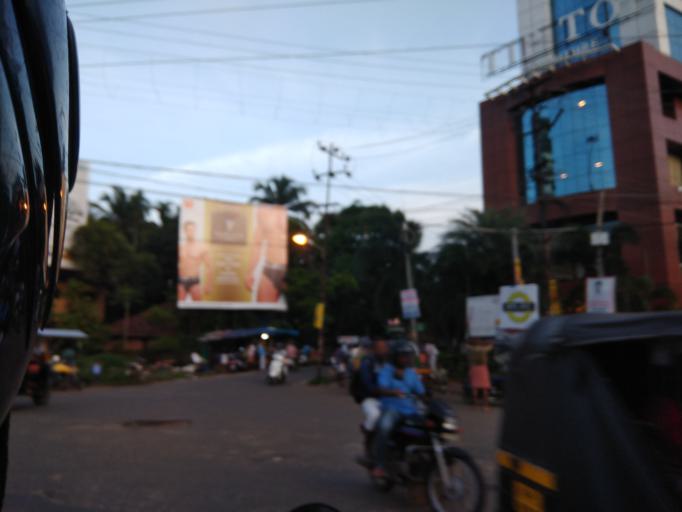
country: IN
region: Kerala
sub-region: Thrissur District
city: Trichur
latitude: 10.5221
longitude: 76.2021
